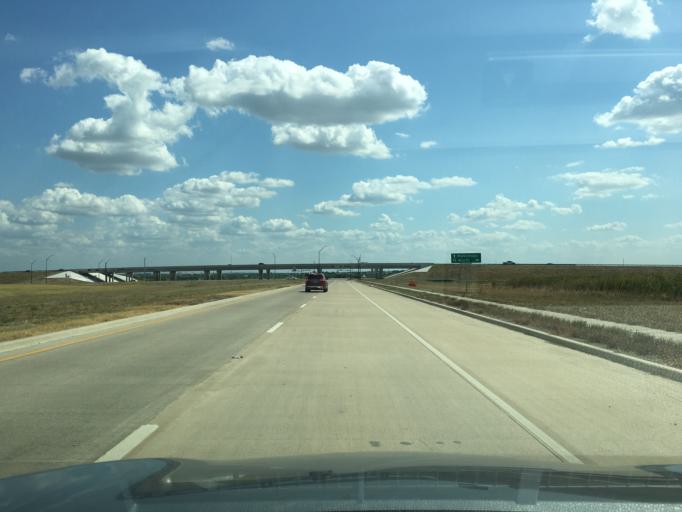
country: US
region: Texas
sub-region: Tarrant County
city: Mansfield
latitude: 32.5259
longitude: -97.0830
